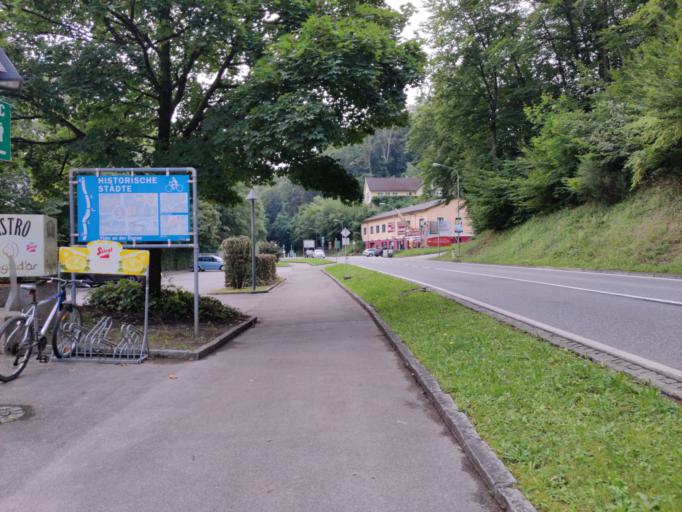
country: AT
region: Lower Austria
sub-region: Politischer Bezirk Melk
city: Ybbs an der Donau
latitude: 48.1875
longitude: 15.0679
